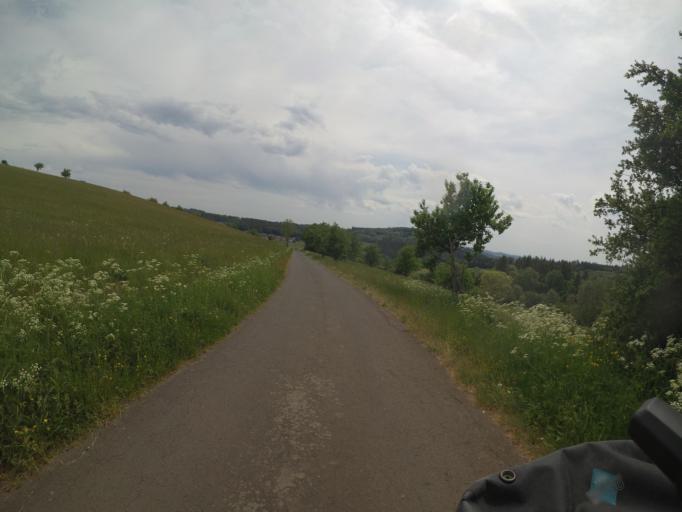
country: DE
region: Rheinland-Pfalz
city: Dockweiler
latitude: 50.2293
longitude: 6.7841
